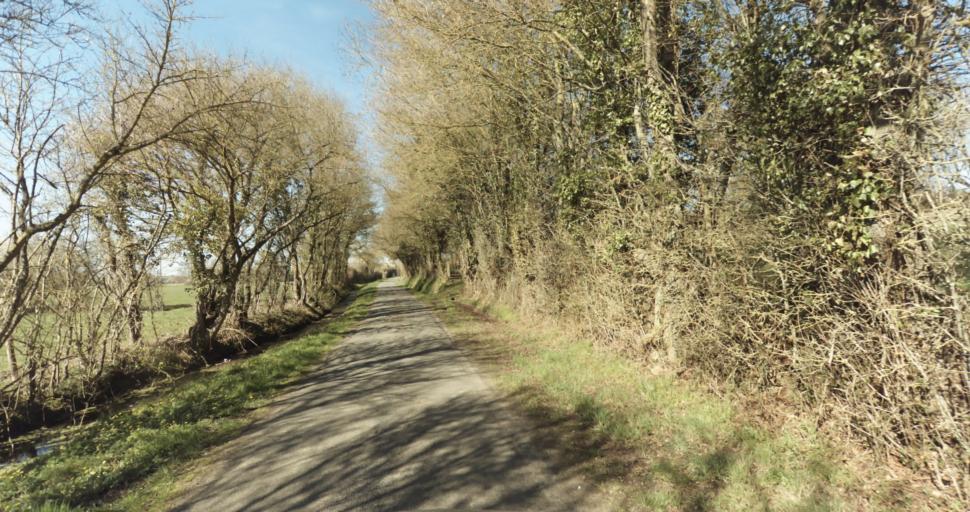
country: FR
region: Lower Normandy
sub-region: Departement du Calvados
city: Saint-Pierre-sur-Dives
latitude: 49.0570
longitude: -0.0246
